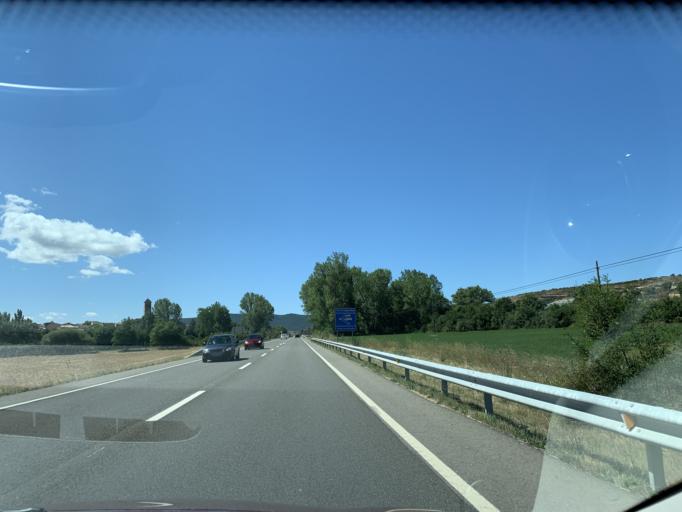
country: ES
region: Aragon
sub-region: Provincia de Huesca
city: Sabinanigo
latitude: 42.5533
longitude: -0.3417
